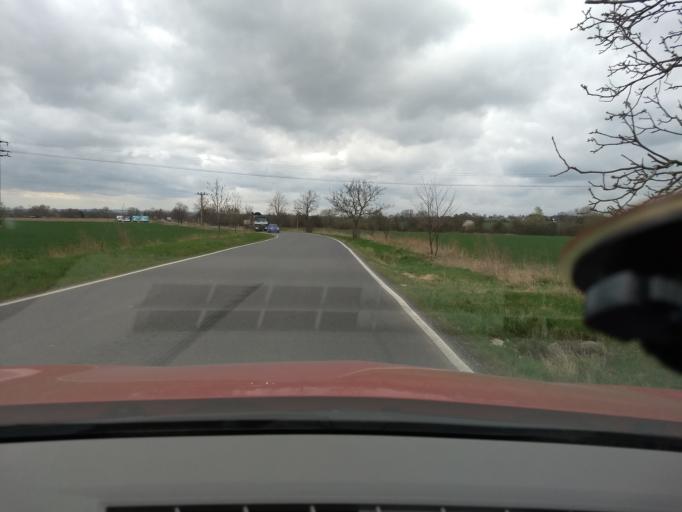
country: CZ
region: Central Bohemia
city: Unhost'
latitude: 50.0613
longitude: 14.1653
